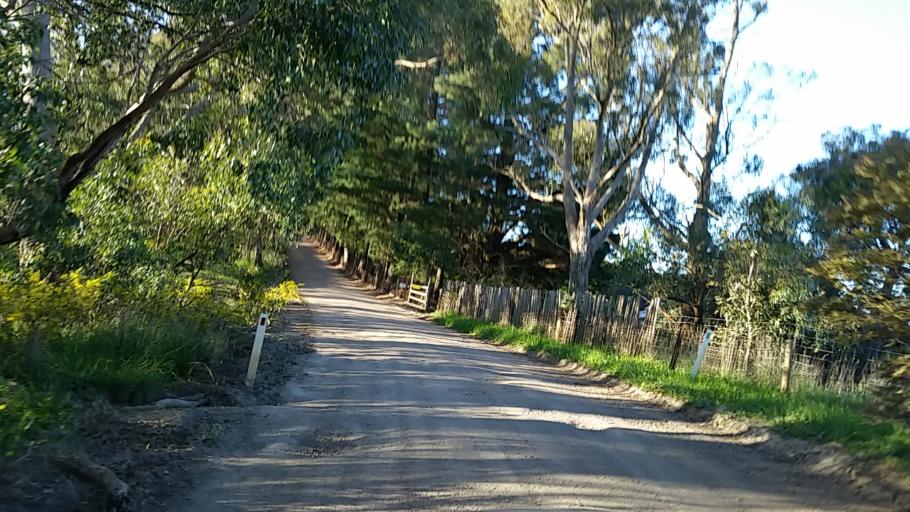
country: AU
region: South Australia
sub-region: Mount Barker
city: Meadows
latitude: -35.2310
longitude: 138.7467
